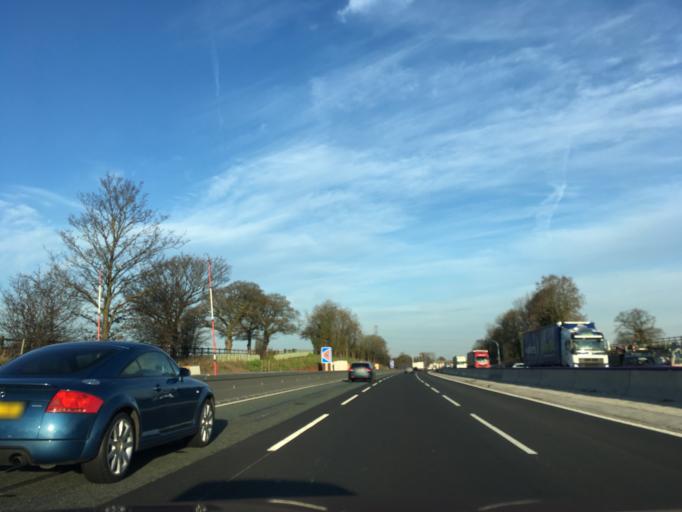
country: GB
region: England
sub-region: Cheshire East
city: Alsager
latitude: 53.0883
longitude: -2.3432
